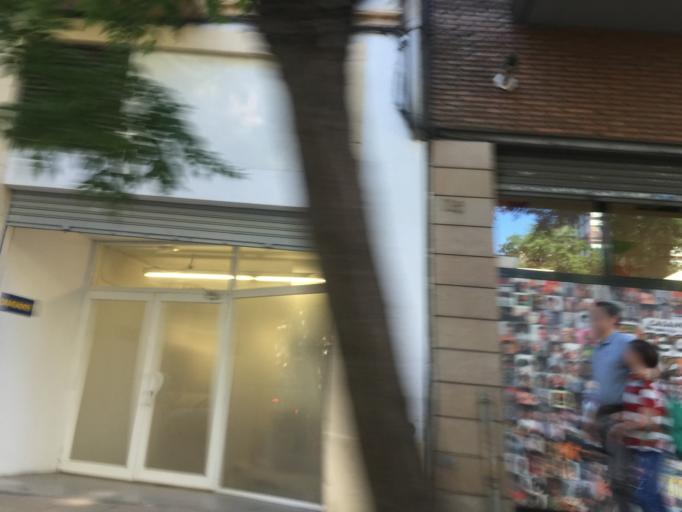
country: ES
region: Catalonia
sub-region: Provincia de Barcelona
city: Sant Marti
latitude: 41.4240
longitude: 2.1911
